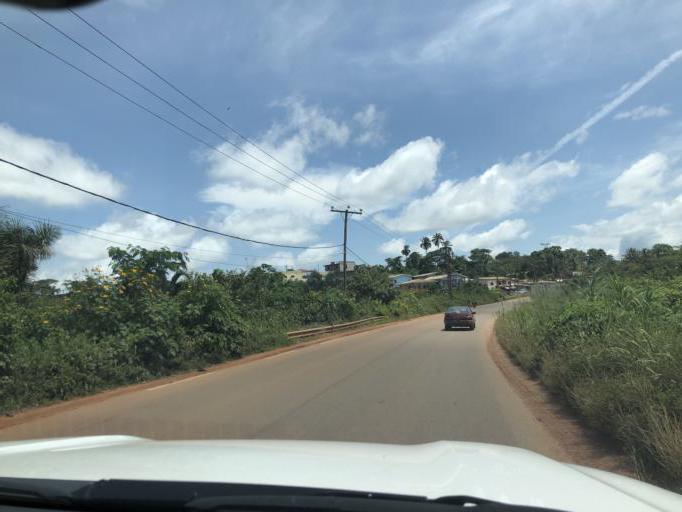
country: CM
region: Centre
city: Yaounde
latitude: 3.8638
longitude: 11.6177
